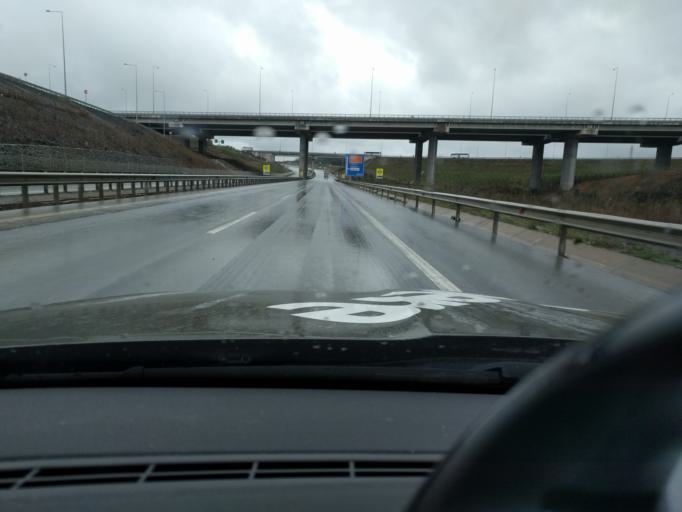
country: TR
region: Istanbul
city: Kemerburgaz
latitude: 41.2306
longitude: 28.8464
